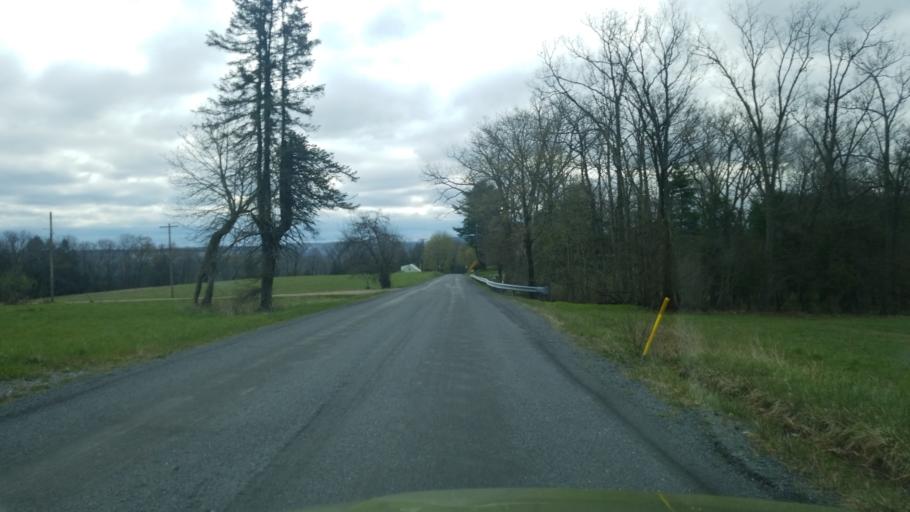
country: US
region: Pennsylvania
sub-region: Clearfield County
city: Clearfield
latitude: 41.0770
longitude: -78.3736
